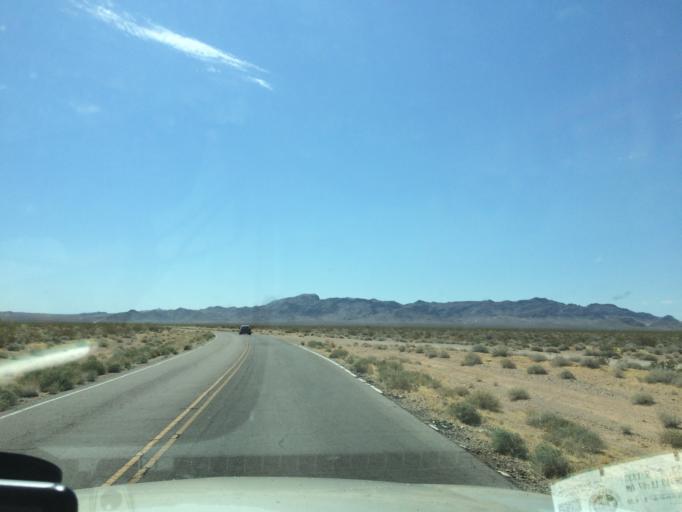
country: US
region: Nevada
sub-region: Clark County
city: Moapa Town
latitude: 36.4594
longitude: -114.7340
